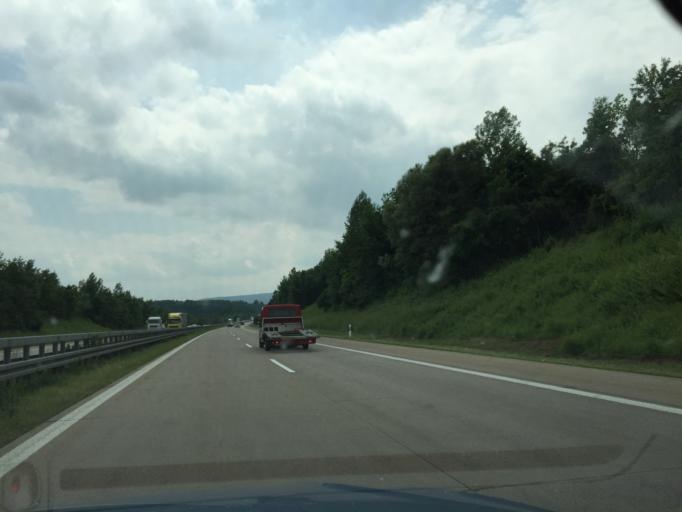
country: DE
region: Baden-Wuerttemberg
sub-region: Regierungsbezirk Stuttgart
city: Westhausen
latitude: 48.9241
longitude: 10.1946
